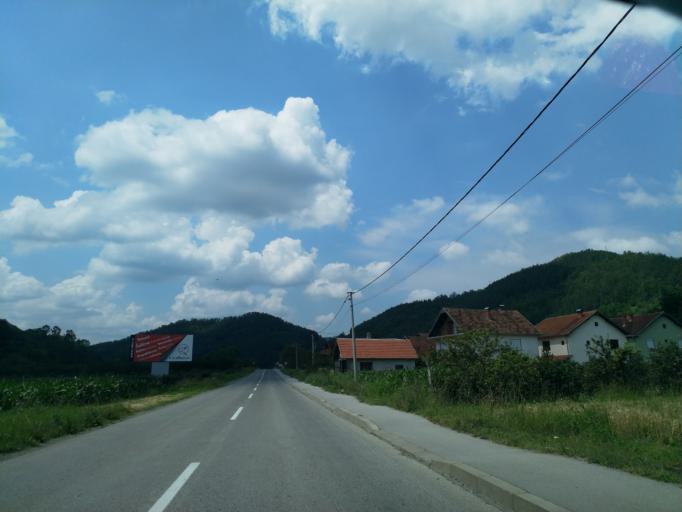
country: RS
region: Central Serbia
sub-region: Rasinski Okrug
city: Aleksandrovac
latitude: 43.3701
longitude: 21.0555
